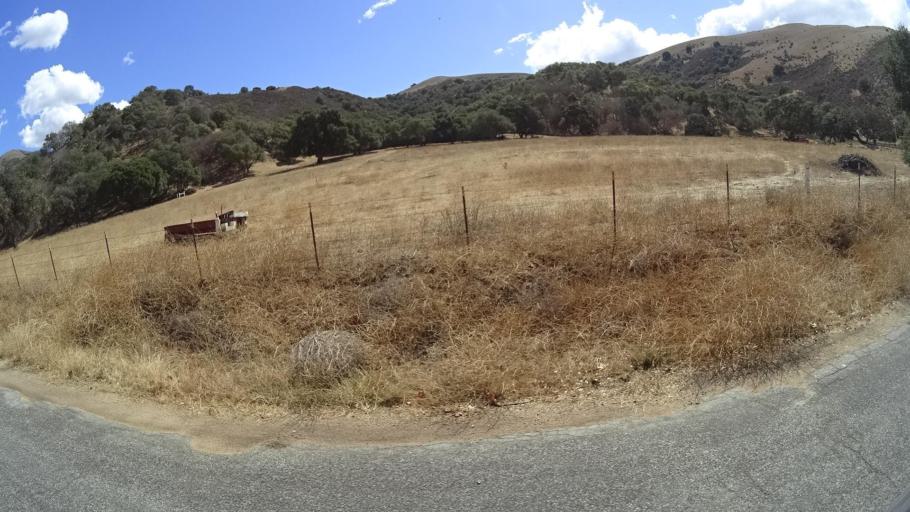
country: US
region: California
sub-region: Monterey County
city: Gonzales
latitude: 36.6041
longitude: -121.4097
